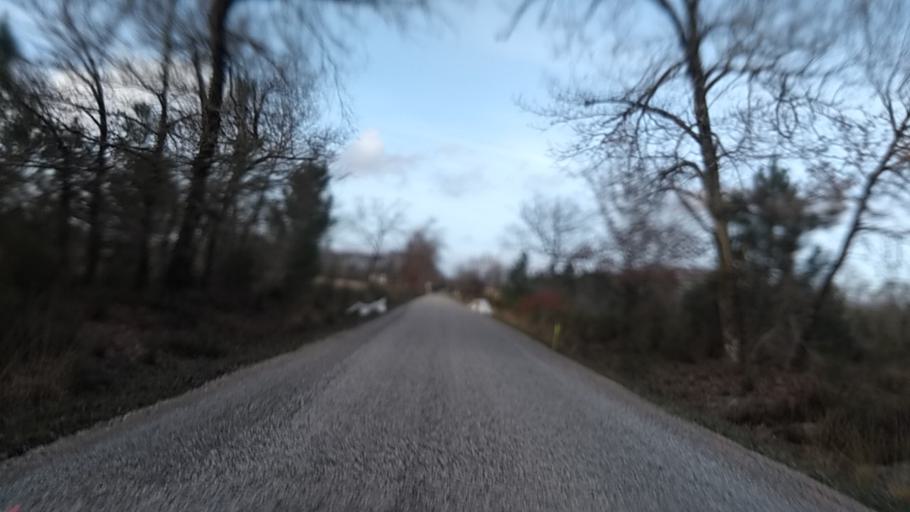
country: FR
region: Aquitaine
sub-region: Departement de la Gironde
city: Le Barp
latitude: 44.5926
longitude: -0.7686
